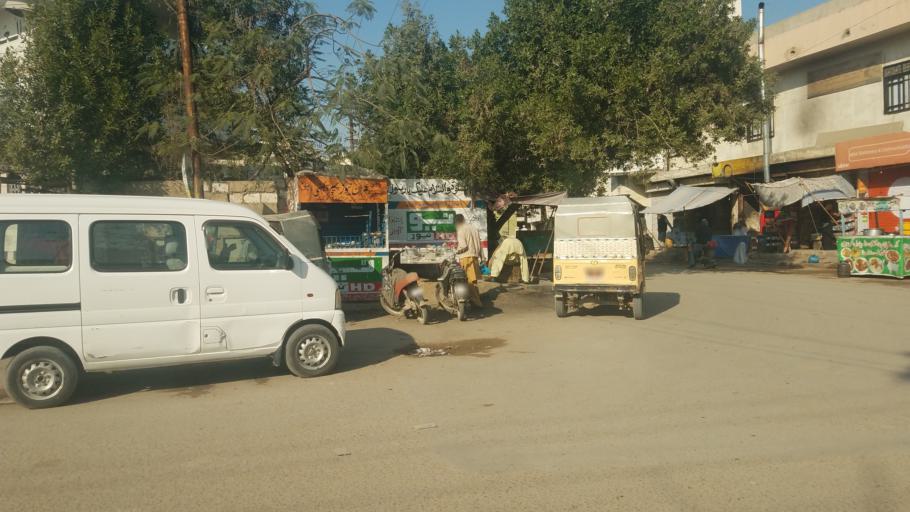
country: PK
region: Sindh
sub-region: Karachi District
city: Karachi
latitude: 24.9380
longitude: 67.0659
